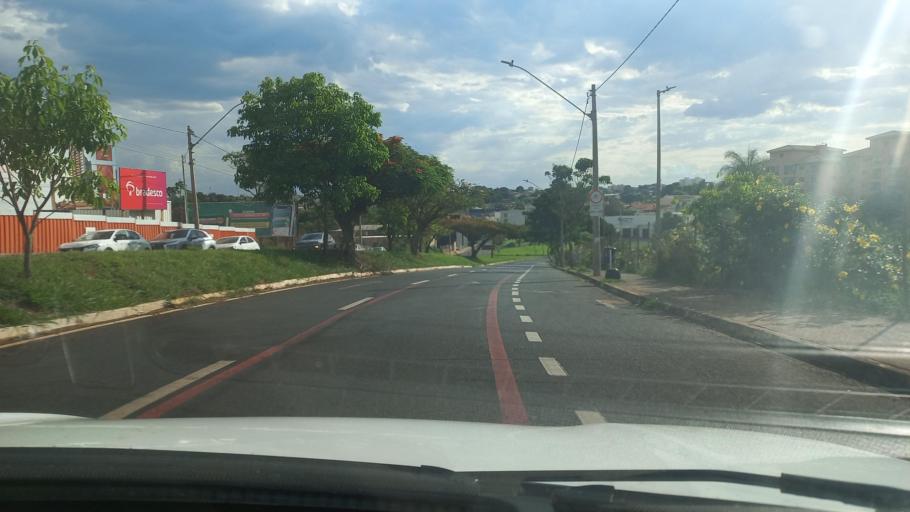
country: BR
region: Minas Gerais
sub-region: Uberaba
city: Uberaba
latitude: -19.7526
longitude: -47.9132
